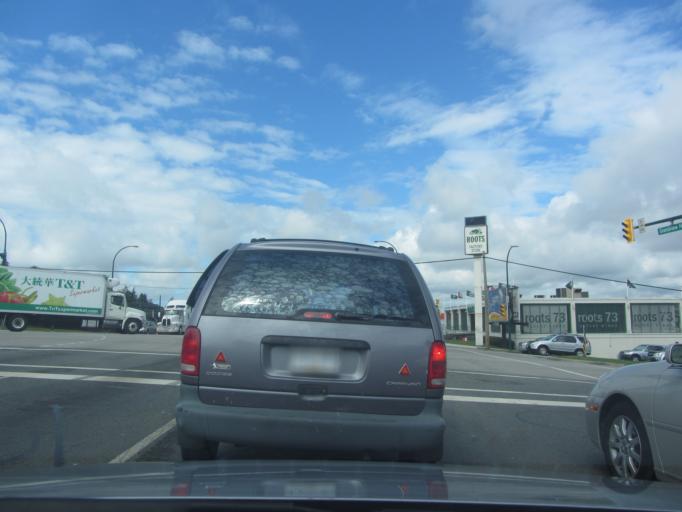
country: CA
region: British Columbia
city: Burnaby
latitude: 49.2582
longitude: -123.0231
